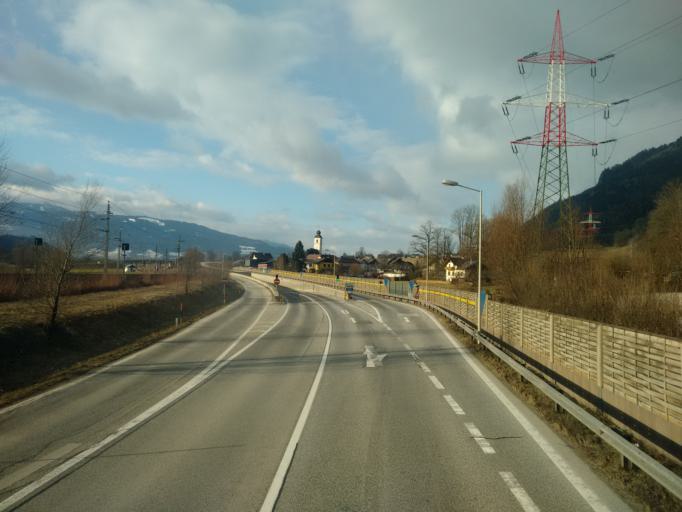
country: AT
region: Styria
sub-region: Politischer Bezirk Liezen
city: Stainach
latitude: 47.5423
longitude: 14.1214
